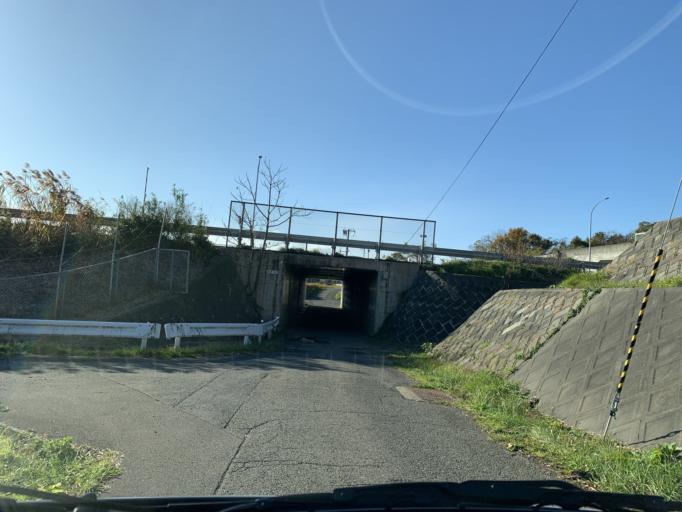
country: JP
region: Iwate
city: Kitakami
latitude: 39.2365
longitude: 141.0800
